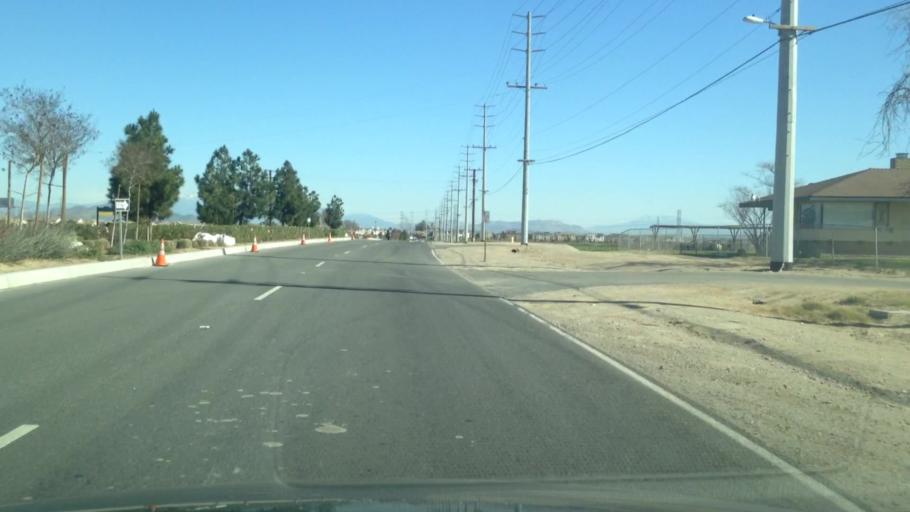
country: US
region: California
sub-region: Riverside County
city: Mira Loma
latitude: 33.9971
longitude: -117.5916
